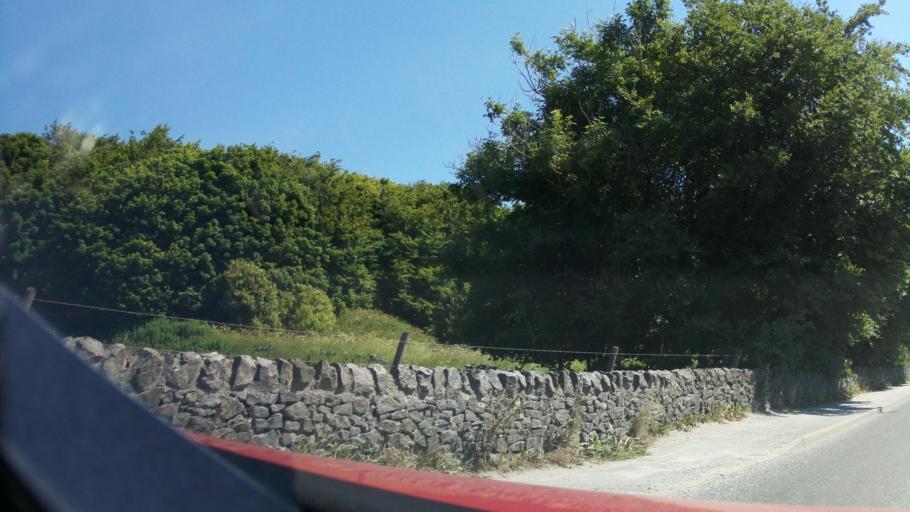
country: GB
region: England
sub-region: Derbyshire
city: Chapel en le Frith
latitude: 53.2978
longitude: -1.8803
